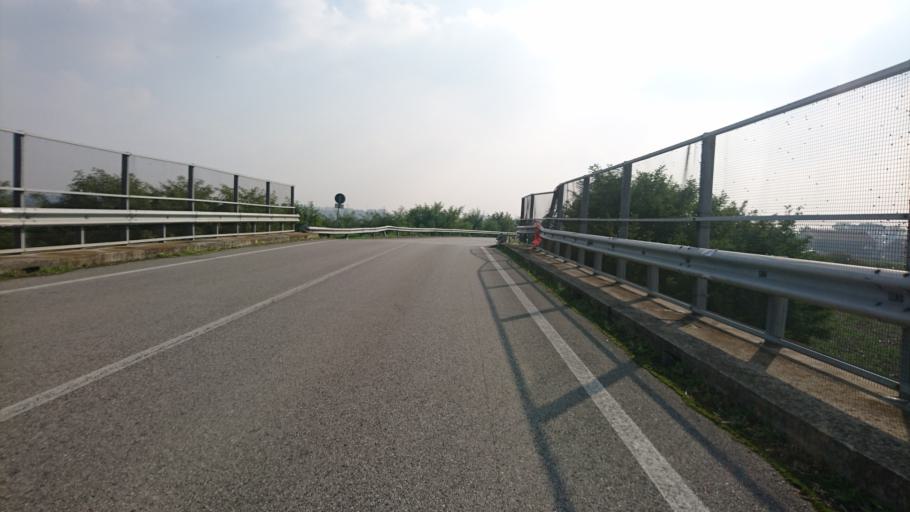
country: IT
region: Veneto
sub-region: Provincia di Rovigo
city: Arqua Polesine
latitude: 45.0253
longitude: 11.7467
